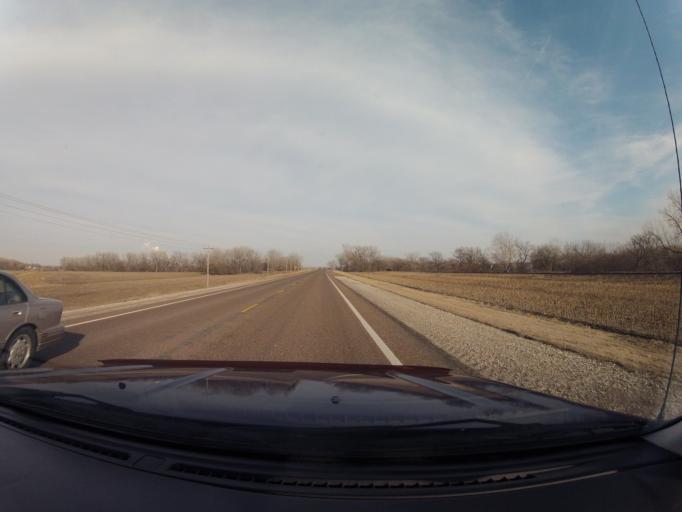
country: US
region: Kansas
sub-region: Pottawatomie County
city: Wamego
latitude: 39.2126
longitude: -96.2397
